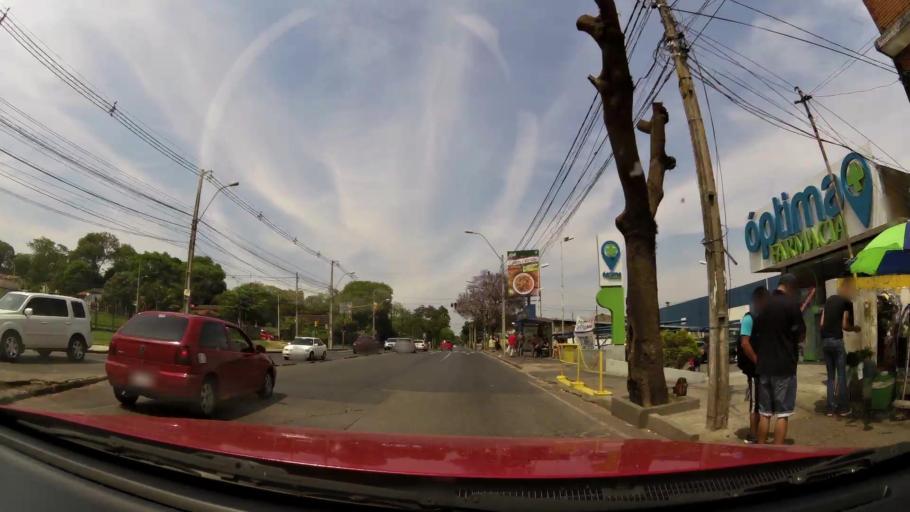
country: PY
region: Asuncion
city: Asuncion
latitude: -25.2721
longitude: -57.5845
